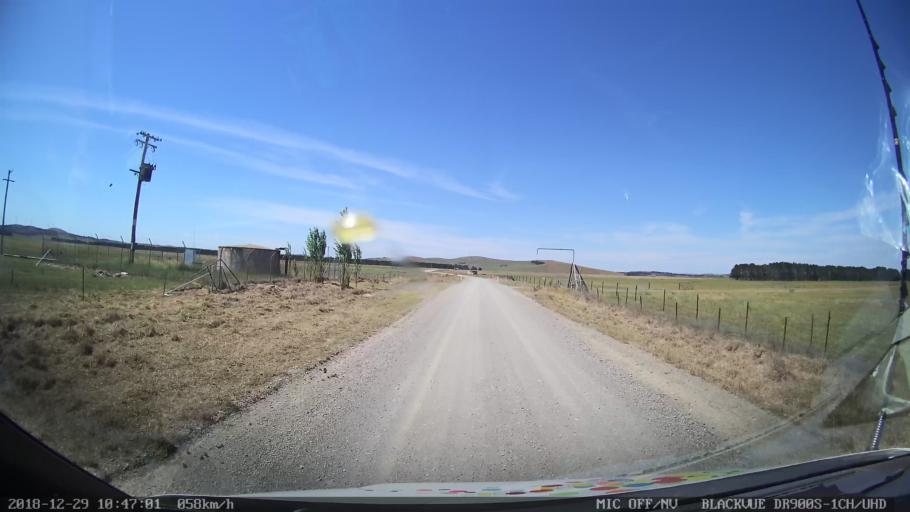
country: AU
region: New South Wales
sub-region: Palerang
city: Bungendore
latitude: -35.0558
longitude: 149.5160
